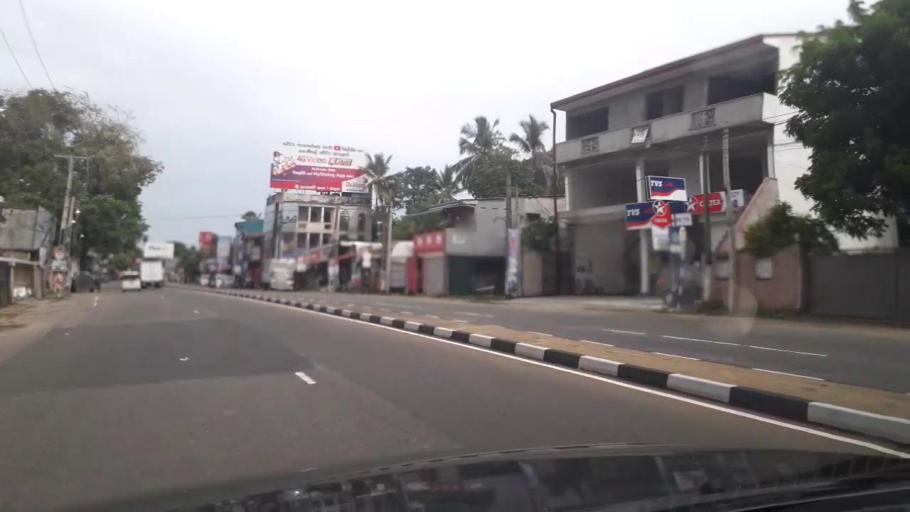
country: LK
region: Western
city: Panadura
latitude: 6.6699
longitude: 79.9277
